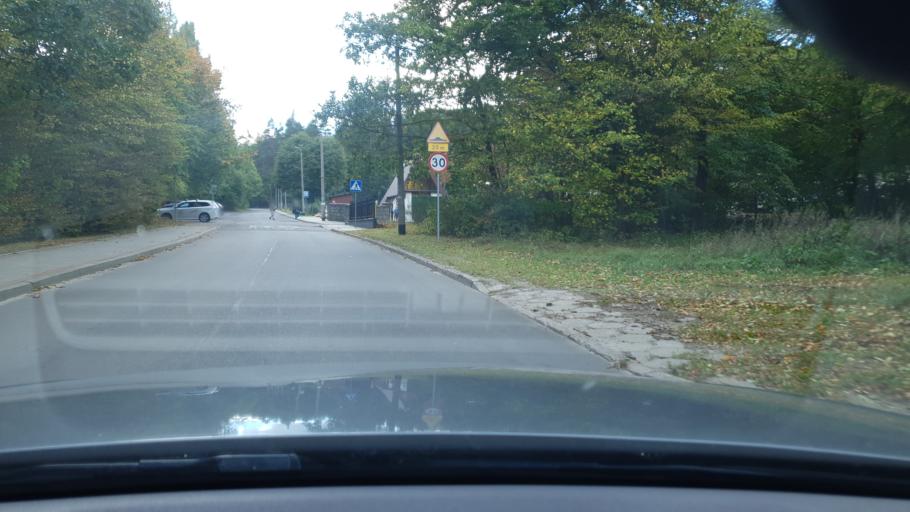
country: PL
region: Pomeranian Voivodeship
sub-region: Powiat wejherowski
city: Reda
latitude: 54.5932
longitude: 18.3374
